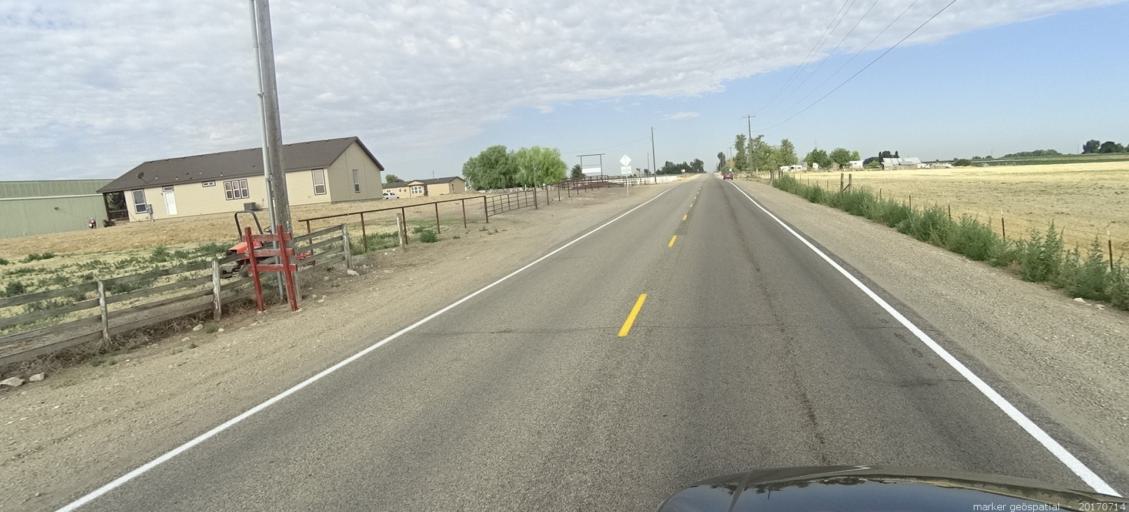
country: US
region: Idaho
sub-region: Ada County
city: Kuna
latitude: 43.4884
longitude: -116.4359
